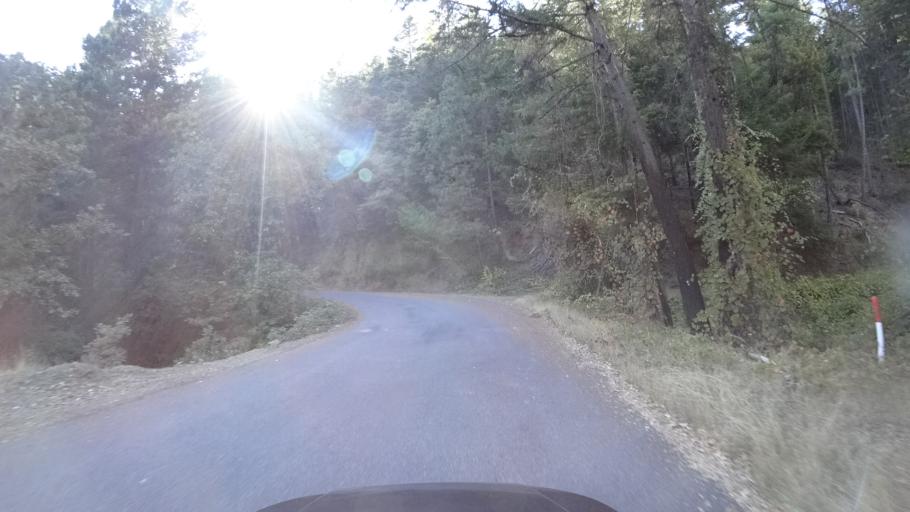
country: US
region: California
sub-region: Humboldt County
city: Willow Creek
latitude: 41.2822
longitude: -123.2655
